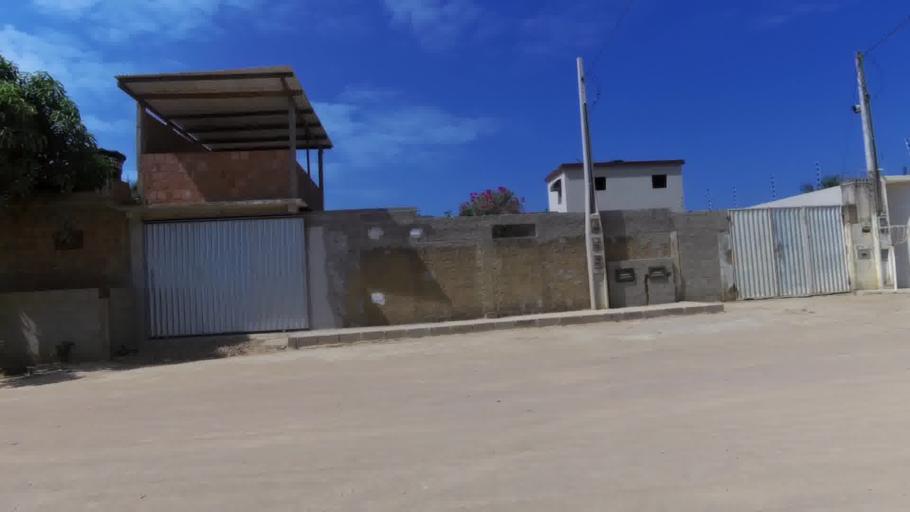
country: BR
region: Espirito Santo
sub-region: Marataizes
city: Marataizes
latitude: -21.0322
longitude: -40.8232
